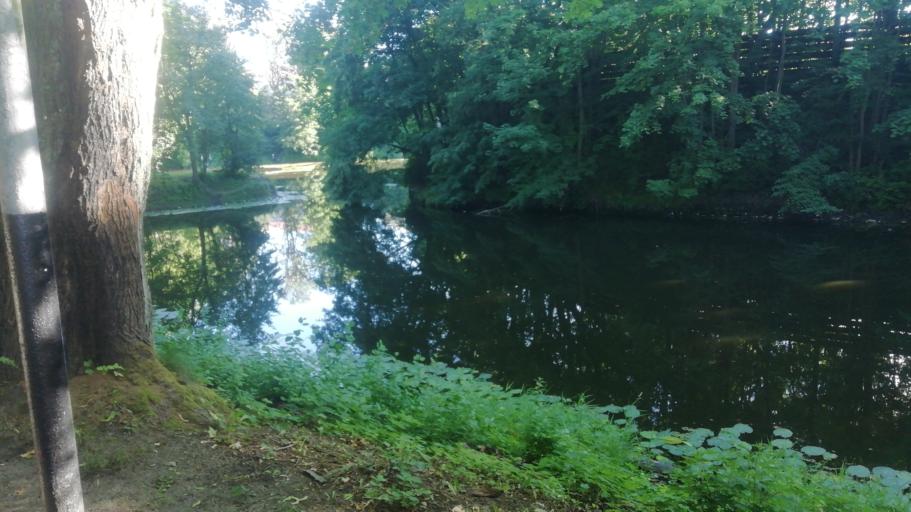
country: RU
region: Kaliningrad
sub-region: Gorod Kaliningrad
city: Kaliningrad
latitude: 54.6938
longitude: 20.5135
